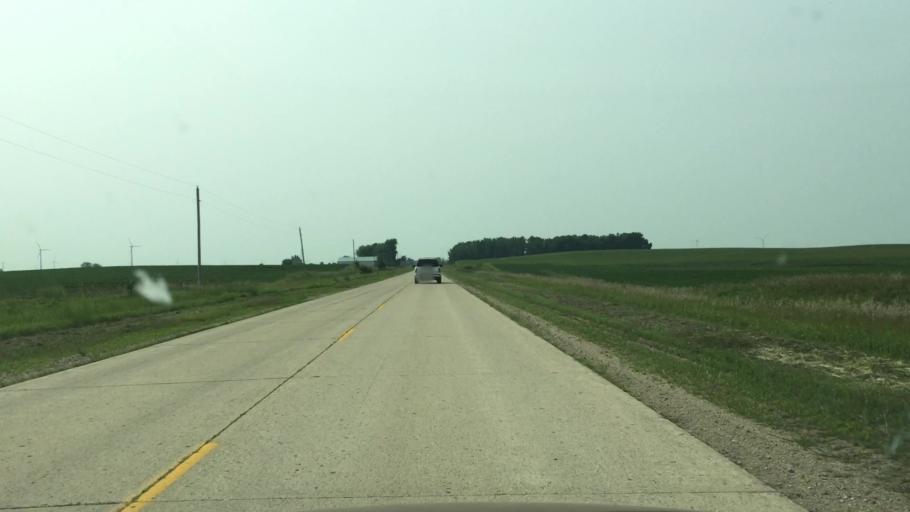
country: US
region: Iowa
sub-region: Dickinson County
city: Lake Park
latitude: 43.4260
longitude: -95.2891
